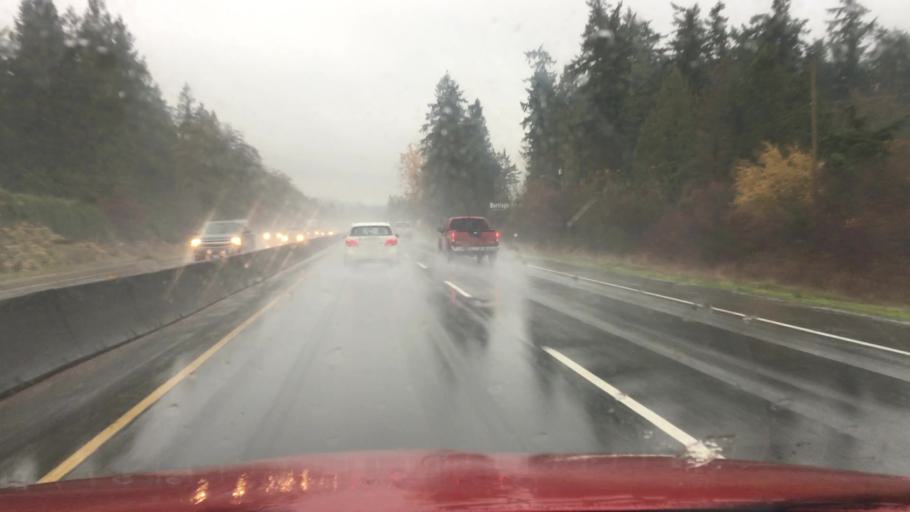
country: CA
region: British Columbia
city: North Saanich
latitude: 48.5784
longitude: -123.3985
